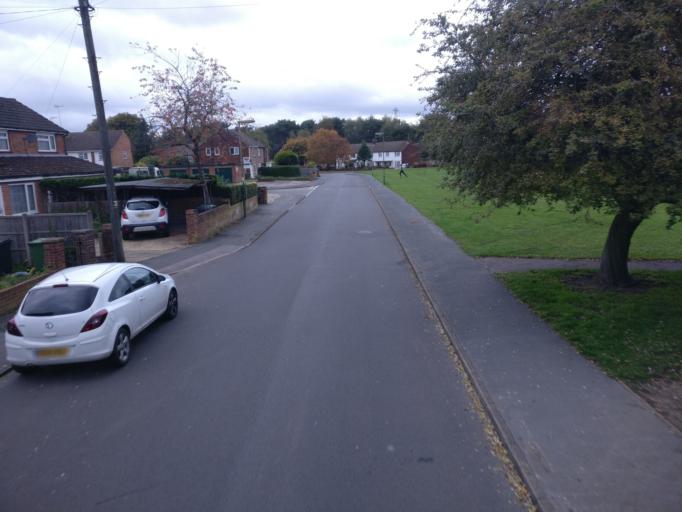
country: GB
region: England
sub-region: Surrey
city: Camberley
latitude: 51.3513
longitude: -0.7249
